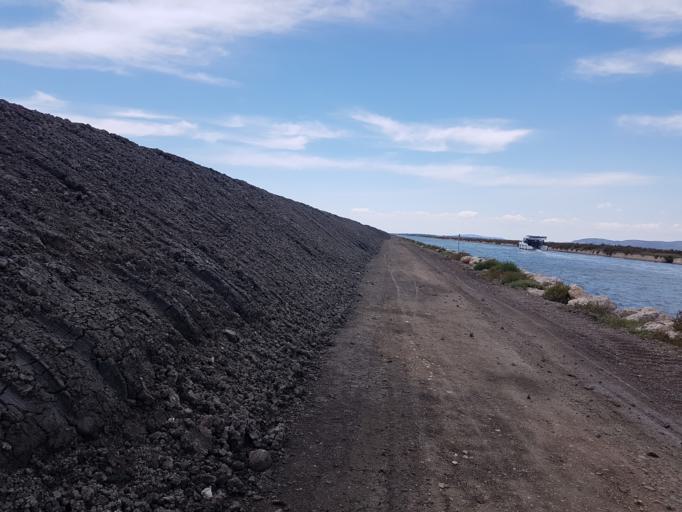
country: FR
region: Languedoc-Roussillon
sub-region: Departement de l'Herault
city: Villeneuve-les-Maguelone
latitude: 43.5061
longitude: 3.8663
